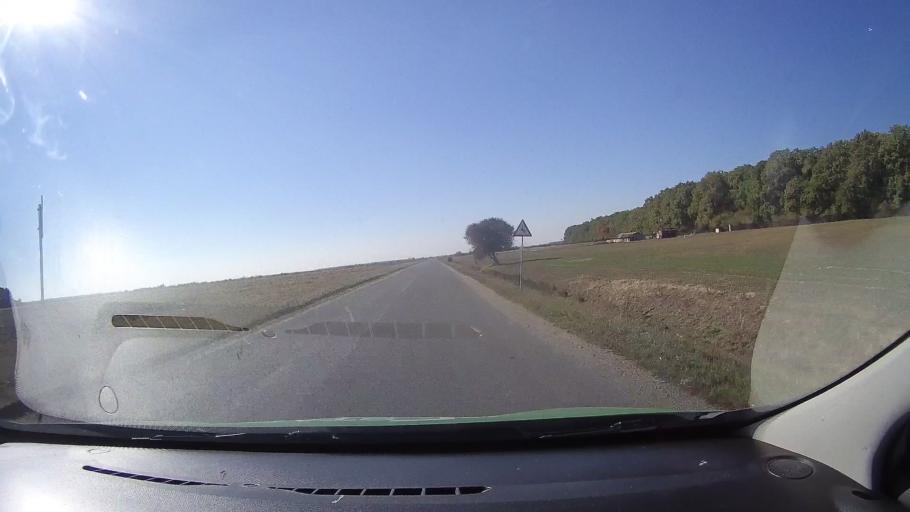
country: RO
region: Satu Mare
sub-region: Municipiul Satu Mare
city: Satmarel
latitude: 47.7026
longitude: 22.7758
